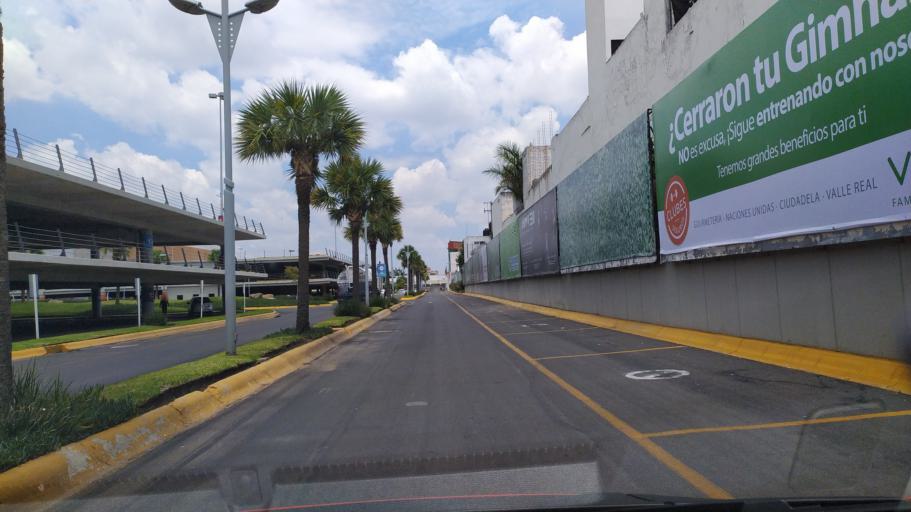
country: MX
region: Jalisco
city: Guadalajara
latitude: 20.6757
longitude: -103.4328
